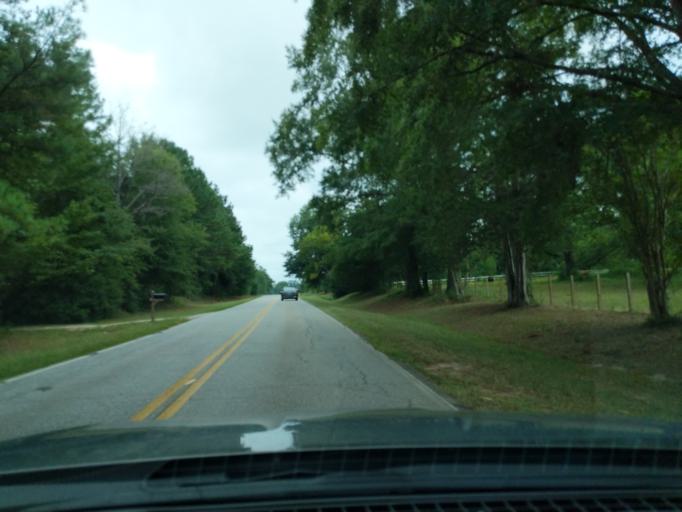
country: US
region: Georgia
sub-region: Columbia County
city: Appling
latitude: 33.6232
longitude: -82.4007
